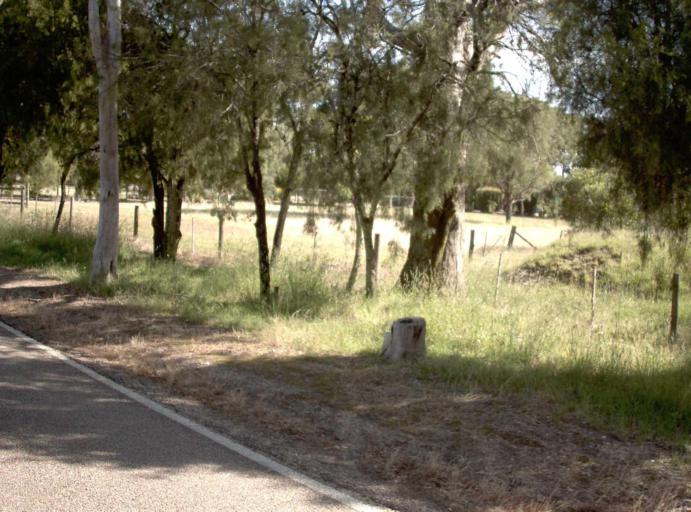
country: AU
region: Victoria
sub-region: East Gippsland
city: Lakes Entrance
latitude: -37.7830
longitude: 147.8264
